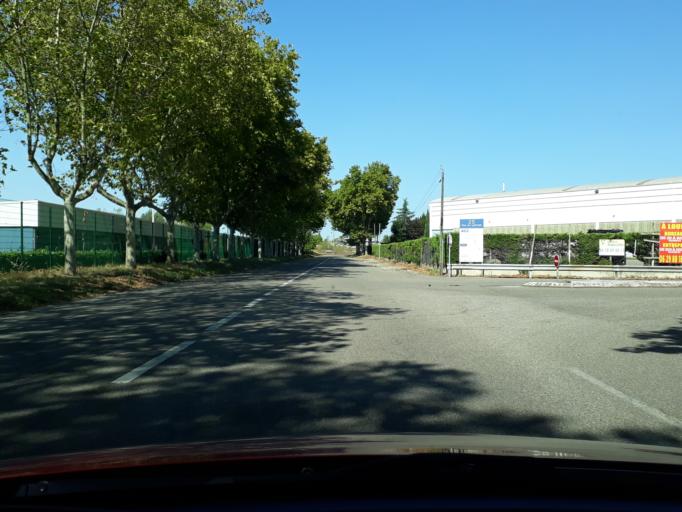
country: FR
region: Rhone-Alpes
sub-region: Departement du Rhone
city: Saint-Priest
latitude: 45.6968
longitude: 4.9149
